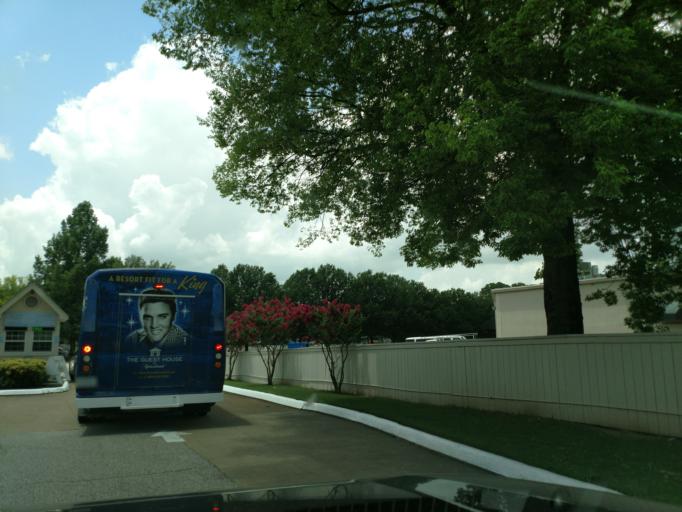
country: US
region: Tennessee
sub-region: Shelby County
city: New South Memphis
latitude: 35.0478
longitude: -90.0256
